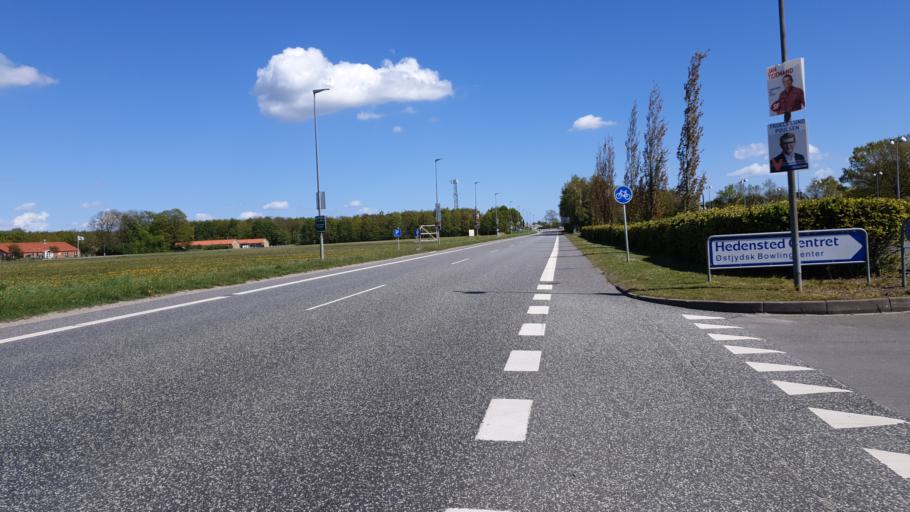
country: DK
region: Central Jutland
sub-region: Hedensted Kommune
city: Hedensted
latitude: 55.7816
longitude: 9.6906
